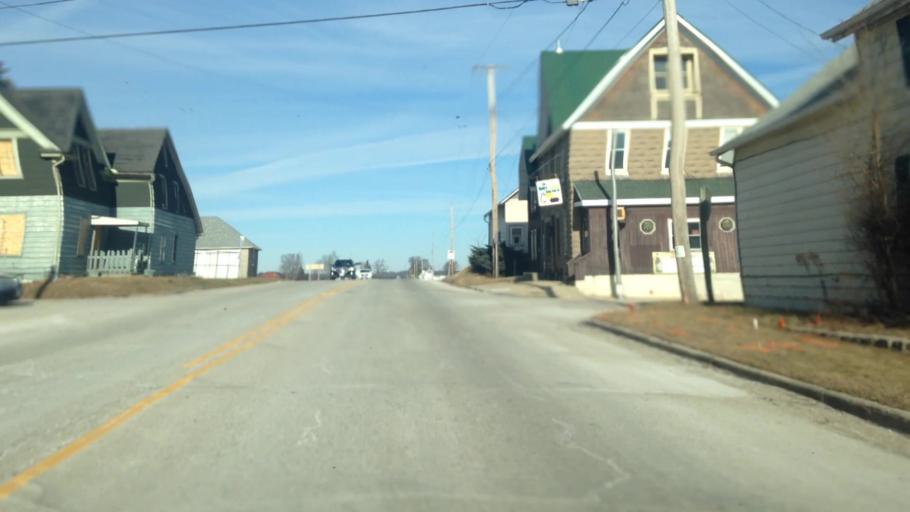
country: US
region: Wisconsin
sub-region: Washington County
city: Richfield
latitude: 43.2656
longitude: -88.2615
